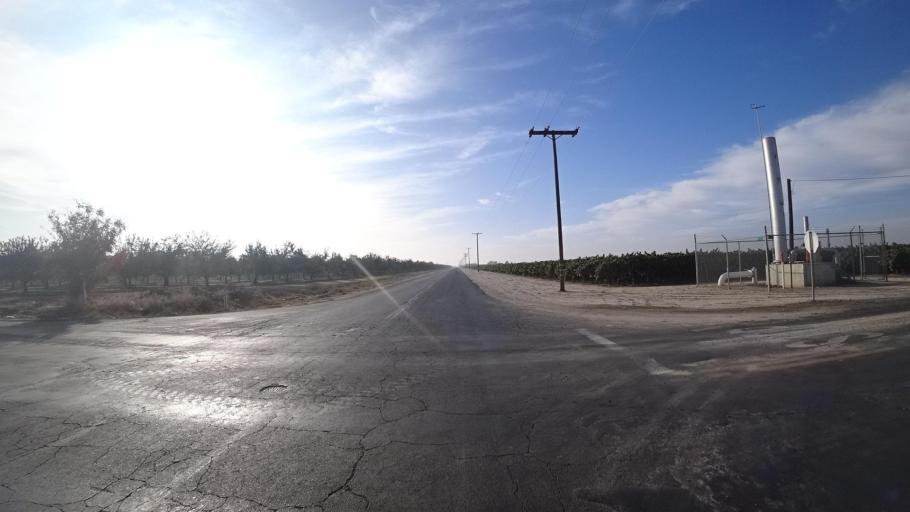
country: US
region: California
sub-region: Kern County
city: McFarland
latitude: 35.6893
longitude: -119.2049
